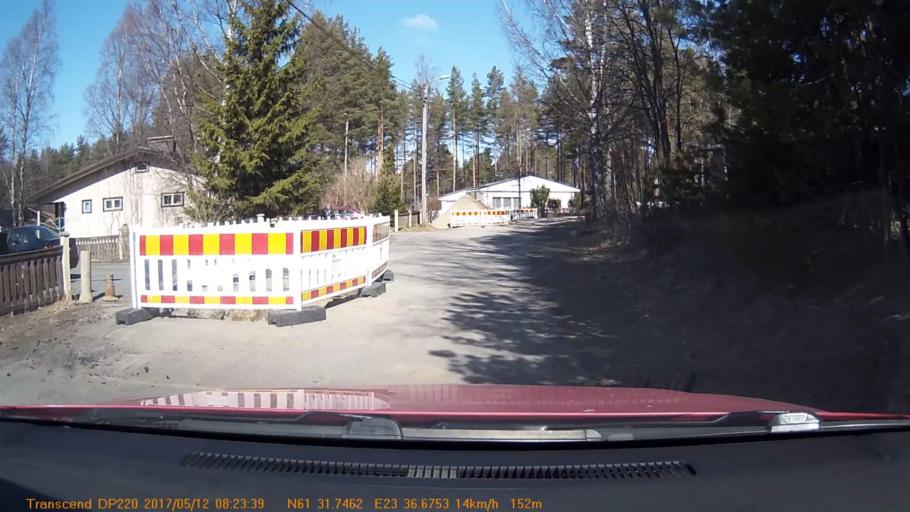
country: FI
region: Pirkanmaa
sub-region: Tampere
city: Yloejaervi
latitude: 61.5290
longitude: 23.6113
